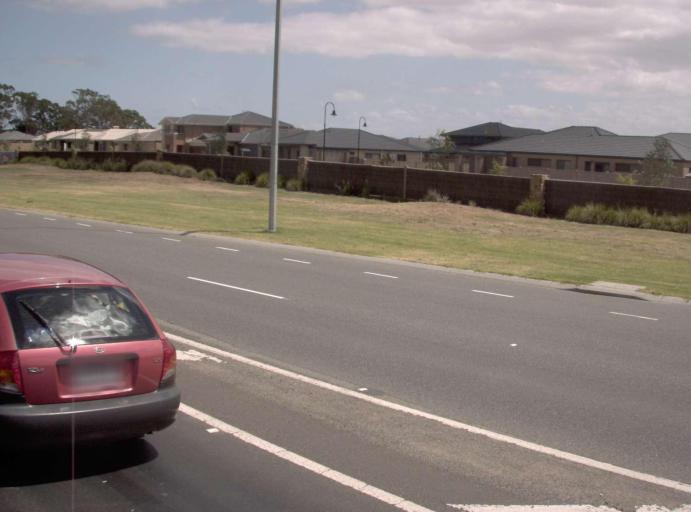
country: AU
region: Victoria
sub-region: Casey
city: Lynbrook
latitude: -38.0781
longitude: 145.2431
